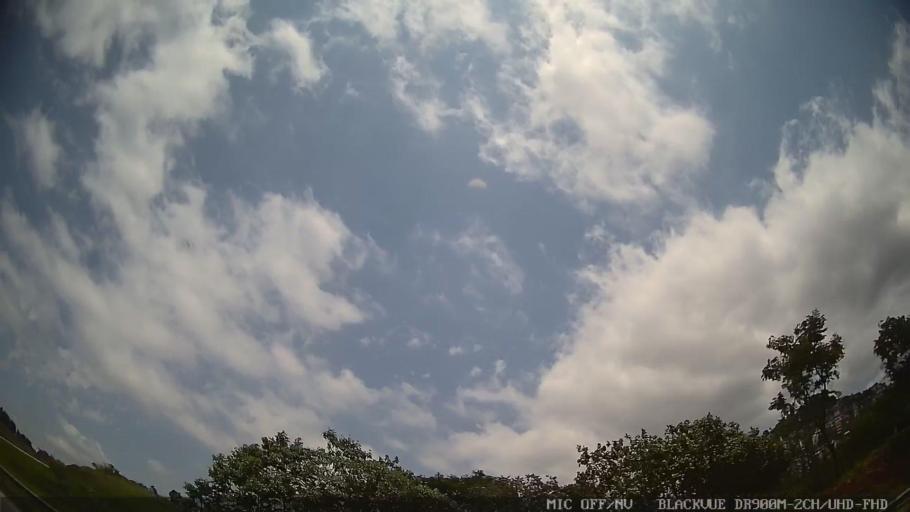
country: BR
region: Sao Paulo
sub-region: Caieiras
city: Caieiras
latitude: -23.4134
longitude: -46.7352
